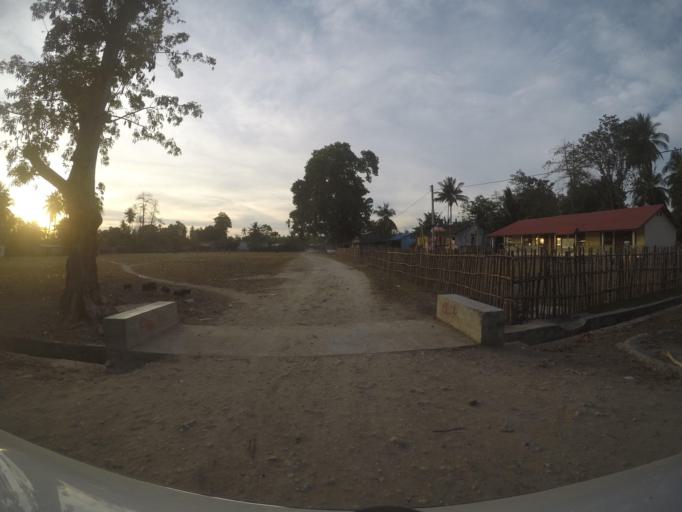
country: TL
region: Viqueque
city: Viqueque
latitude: -8.9451
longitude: 126.4489
